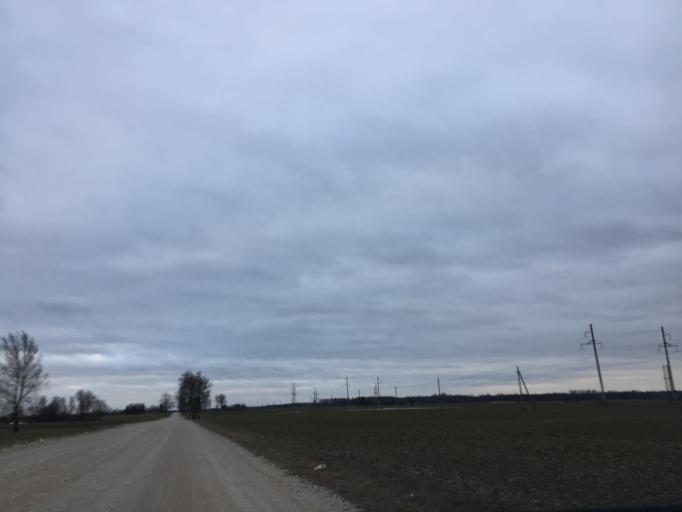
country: LT
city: Zagare
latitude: 56.3426
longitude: 23.2501
